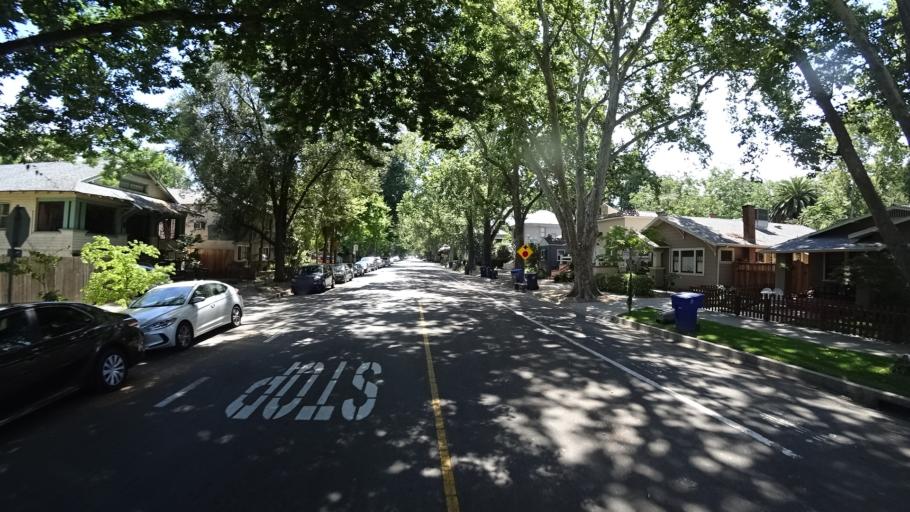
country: US
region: California
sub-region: Sacramento County
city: Sacramento
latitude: 38.5821
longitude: -121.4775
